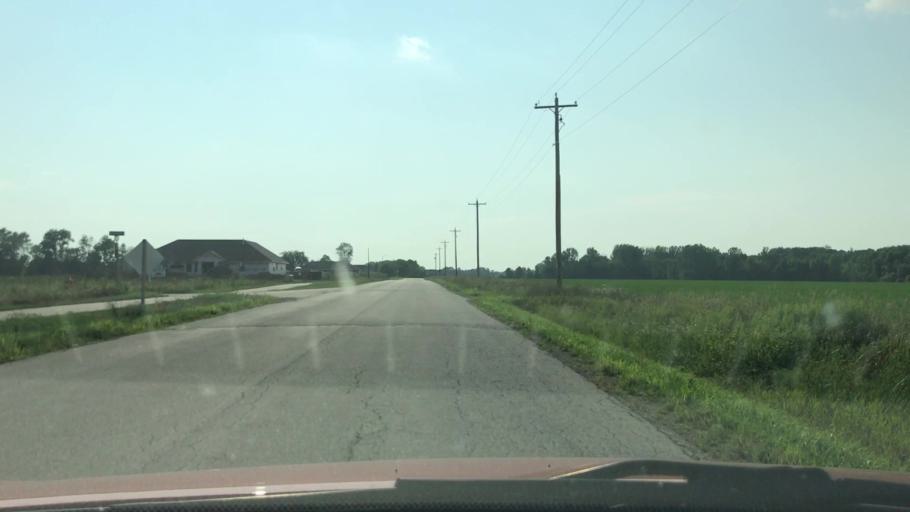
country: US
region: Wisconsin
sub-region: Brown County
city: Oneida
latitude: 44.4297
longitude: -88.1409
